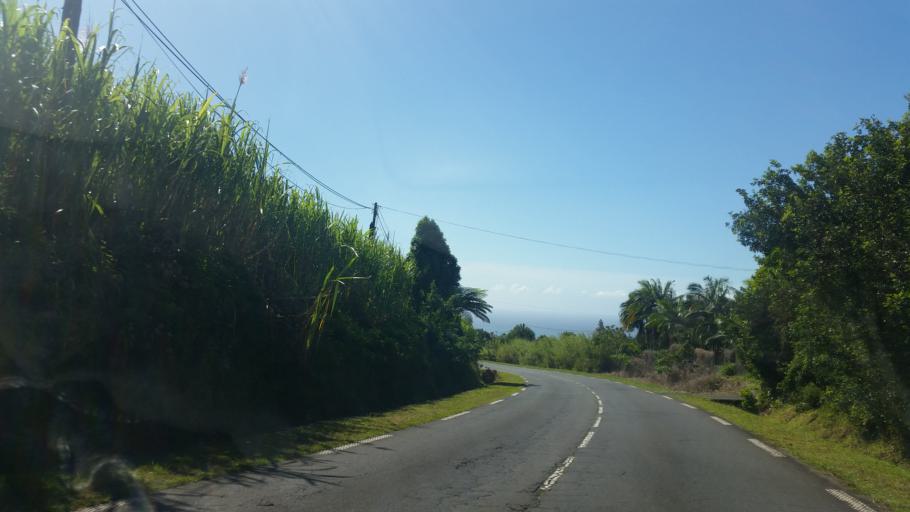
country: RE
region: Reunion
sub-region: Reunion
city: Saint-Benoit
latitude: -21.0888
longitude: 55.6899
